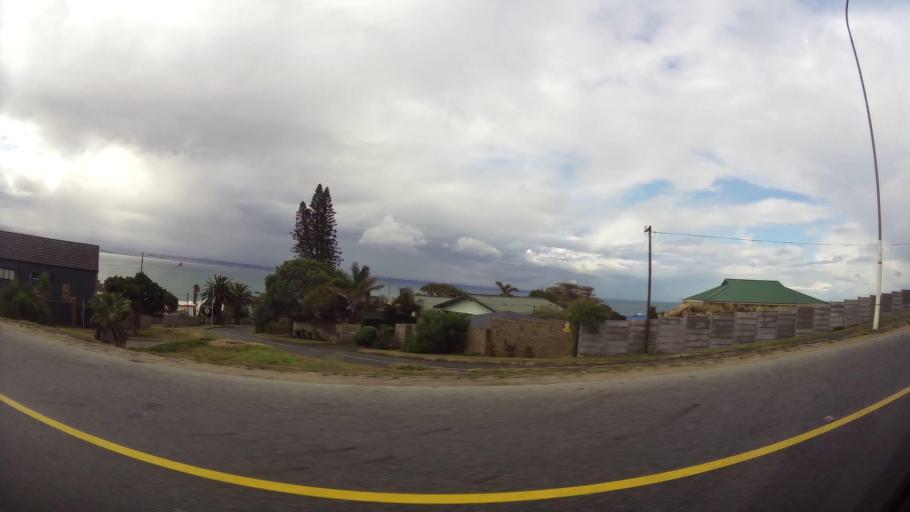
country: ZA
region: Western Cape
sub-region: Eden District Municipality
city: Mossel Bay
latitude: -34.1764
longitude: 22.1316
